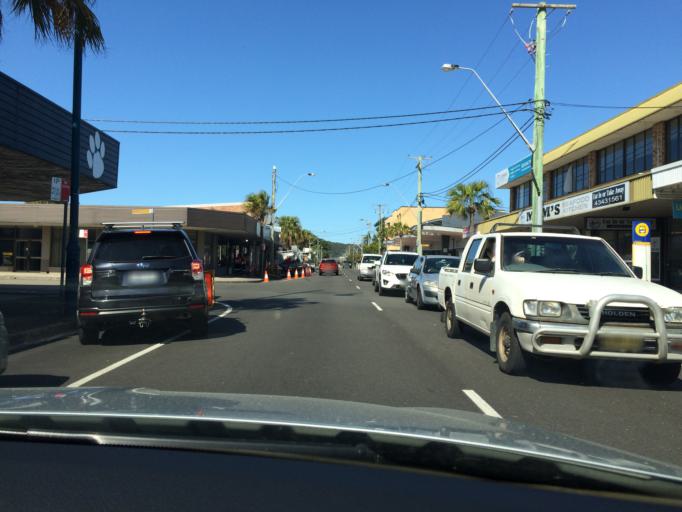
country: AU
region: New South Wales
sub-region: Gosford Shire
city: Umina
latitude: -33.5218
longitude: 151.3216
